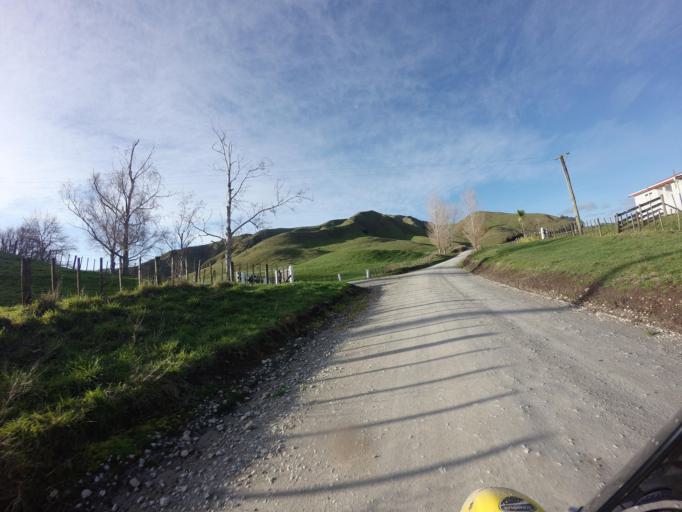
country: NZ
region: Hawke's Bay
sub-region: Wairoa District
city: Wairoa
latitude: -38.7204
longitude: 177.5719
